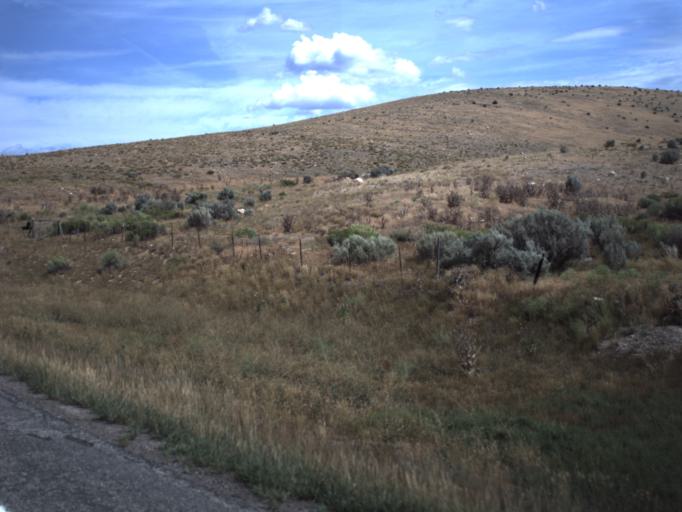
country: US
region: Utah
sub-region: Sanpete County
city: Fairview
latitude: 39.8178
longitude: -111.5074
